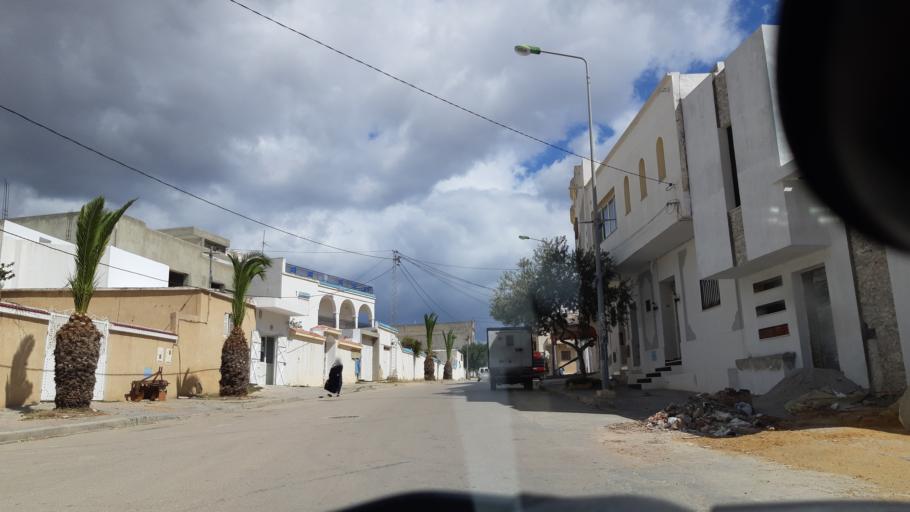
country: TN
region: Susah
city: Akouda
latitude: 35.8771
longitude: 10.5426
